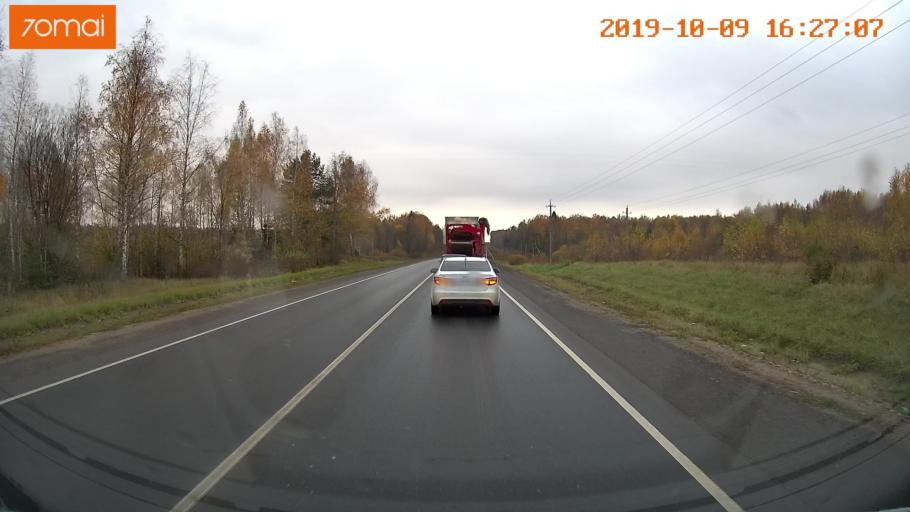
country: RU
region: Kostroma
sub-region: Kostromskoy Rayon
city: Kostroma
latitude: 57.6345
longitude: 40.9269
